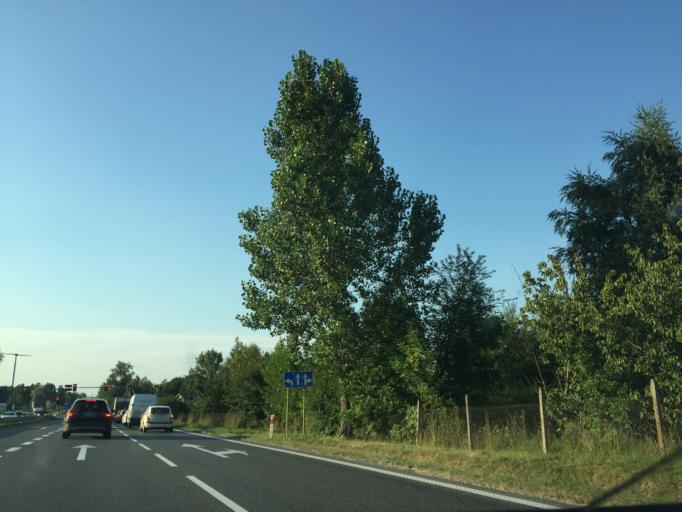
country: PL
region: Masovian Voivodeship
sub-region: Powiat piaseczynski
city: Tarczyn
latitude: 51.9570
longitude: 20.8388
